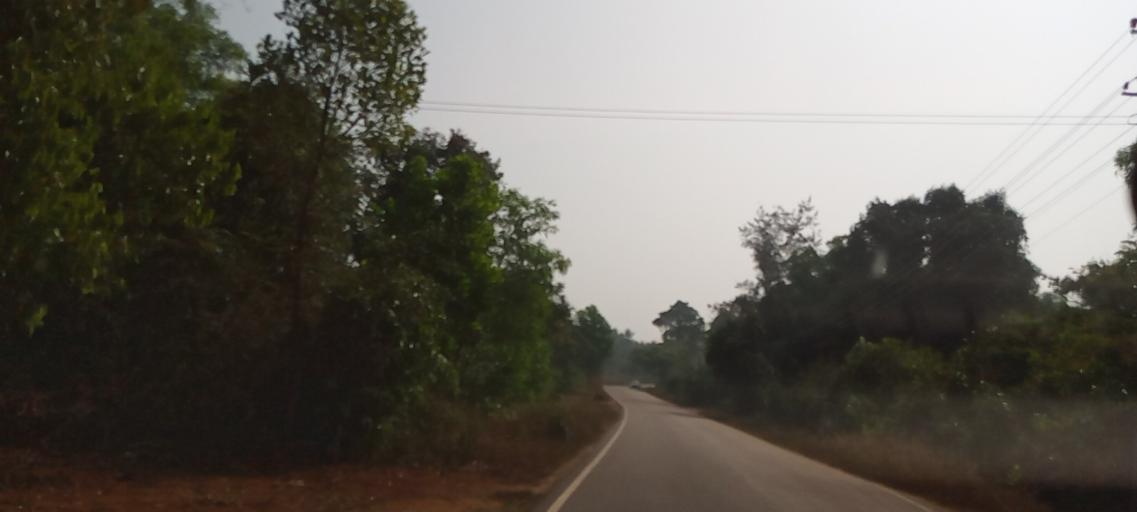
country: IN
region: Karnataka
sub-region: Udupi
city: Coondapoor
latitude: 13.5134
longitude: 74.8025
